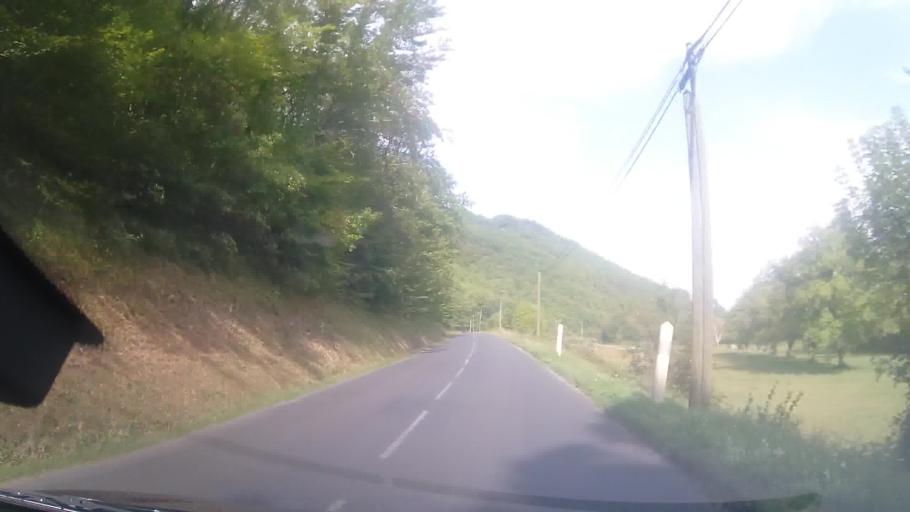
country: FR
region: Aquitaine
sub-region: Departement de la Dordogne
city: Cenac-et-Saint-Julien
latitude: 44.8037
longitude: 1.1575
